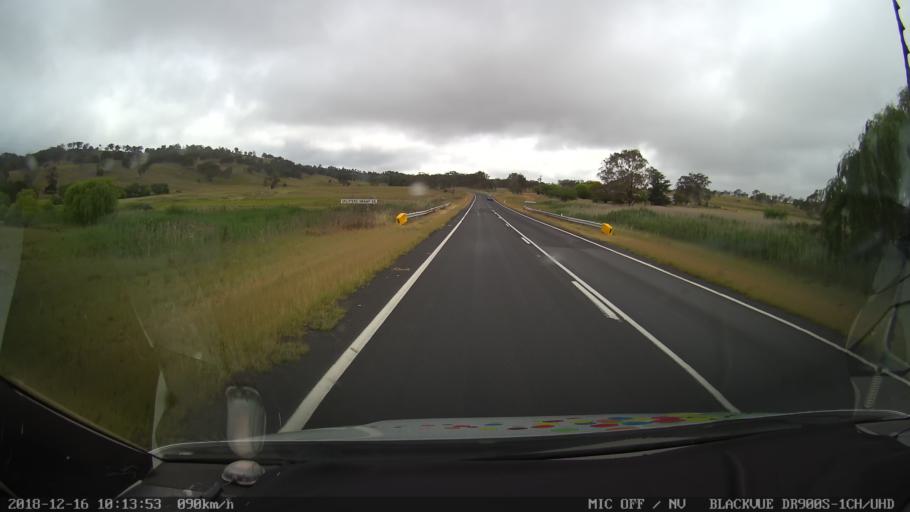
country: AU
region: New South Wales
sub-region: Tenterfield Municipality
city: Carrolls Creek
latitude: -29.2930
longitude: 151.9576
